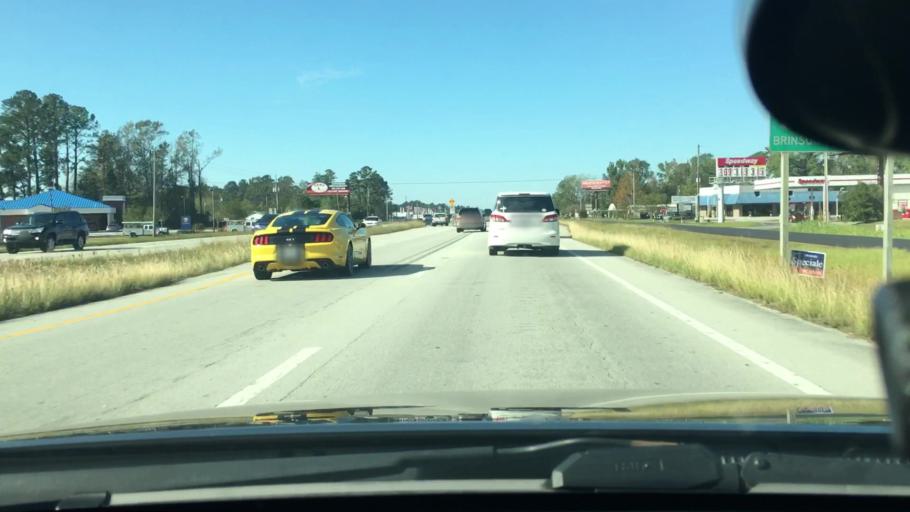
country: US
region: North Carolina
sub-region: Craven County
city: James City
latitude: 35.0638
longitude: -77.0218
